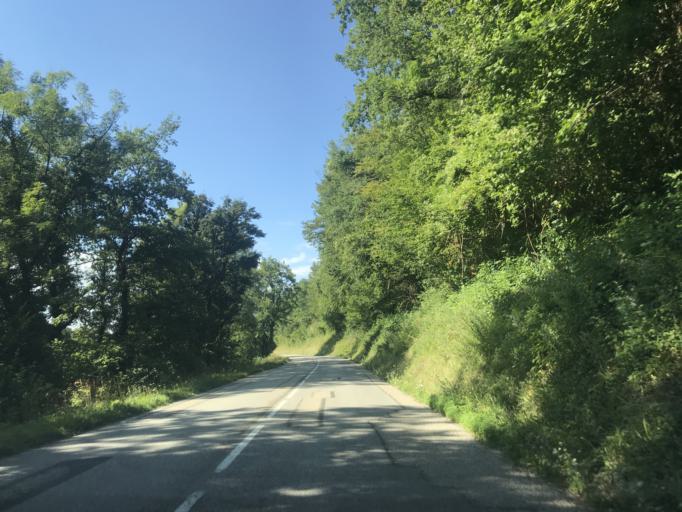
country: FR
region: Rhone-Alpes
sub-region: Departement de la Savoie
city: Yenne
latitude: 45.7650
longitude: 5.7844
